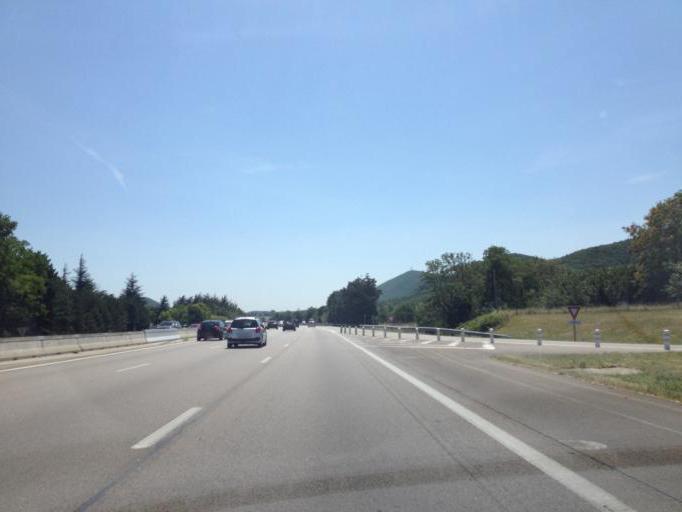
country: FR
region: Rhone-Alpes
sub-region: Departement de l'Ardeche
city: Cruas
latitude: 44.6454
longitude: 4.7921
